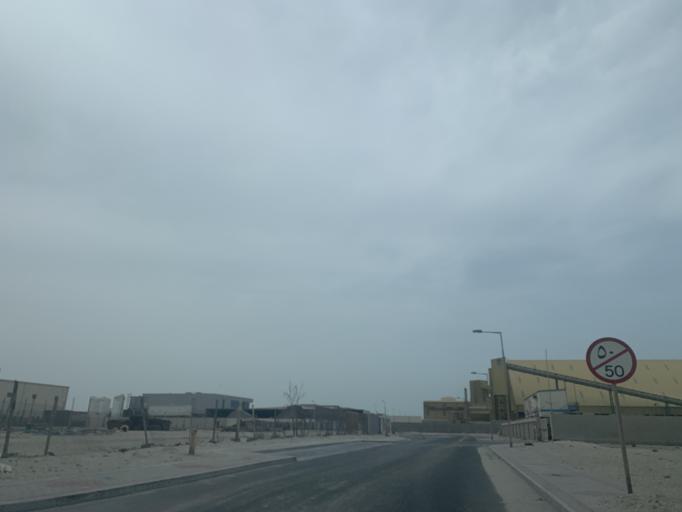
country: BH
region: Muharraq
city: Al Hadd
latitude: 26.2135
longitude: 50.6824
